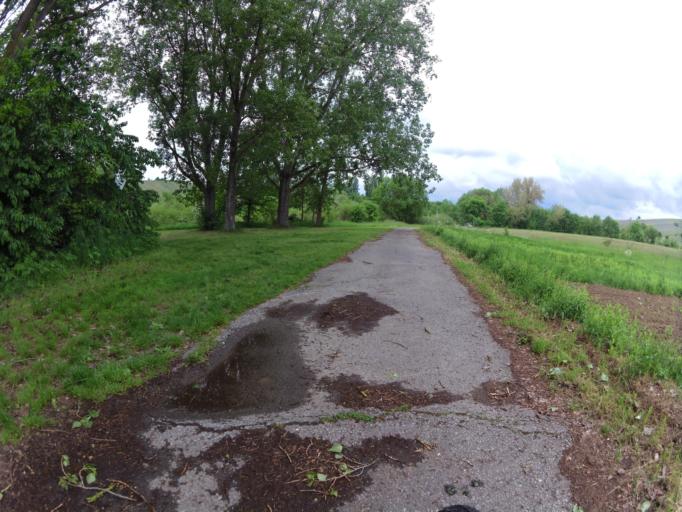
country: DE
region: Bavaria
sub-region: Regierungsbezirk Unterfranken
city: Sommerach
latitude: 49.8294
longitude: 10.1930
